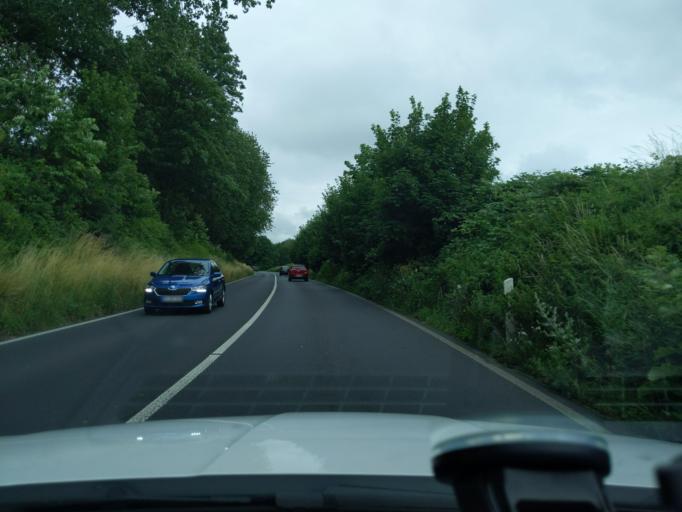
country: DE
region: North Rhine-Westphalia
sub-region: Regierungsbezirk Dusseldorf
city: Erkrath
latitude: 51.2577
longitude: 6.9191
